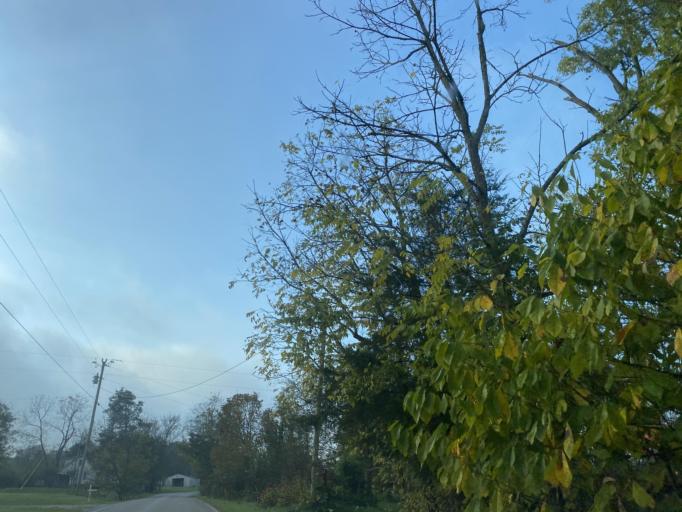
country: US
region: Kentucky
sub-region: Pendleton County
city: Falmouth
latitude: 38.7335
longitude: -84.3162
